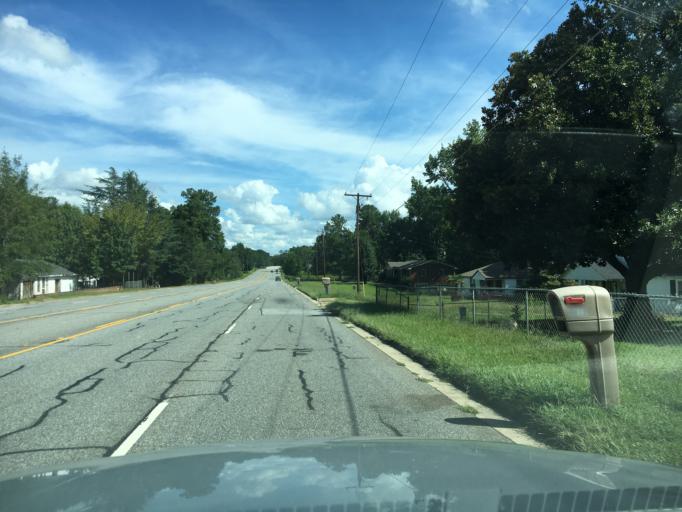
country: US
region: South Carolina
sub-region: Greenwood County
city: Ware Shoals
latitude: 34.4383
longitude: -82.2484
